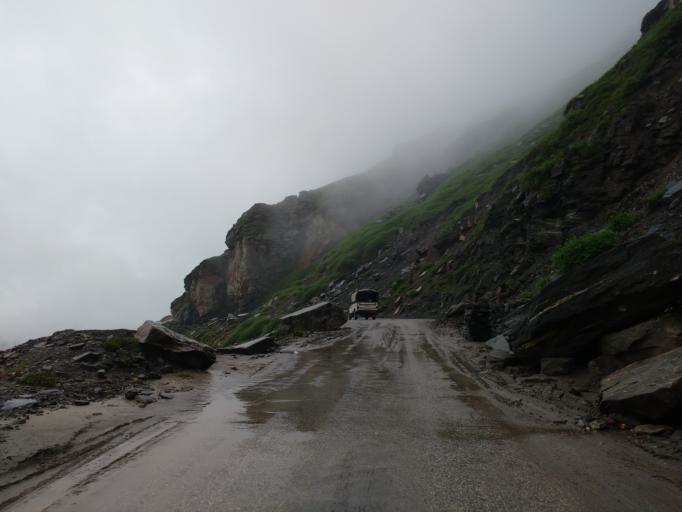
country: IN
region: Himachal Pradesh
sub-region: Kulu
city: Manali
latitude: 32.3566
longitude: 77.2275
